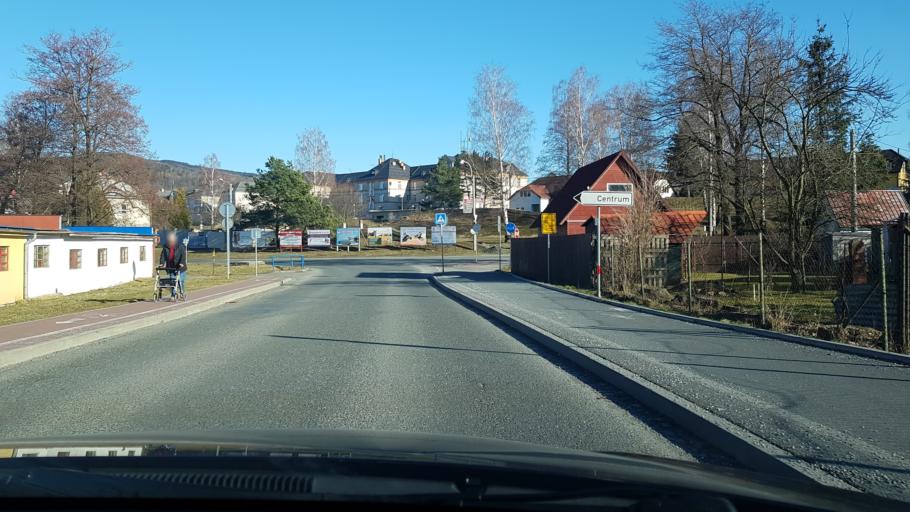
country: CZ
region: Olomoucky
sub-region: Okres Jesenik
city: Jesenik
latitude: 50.2215
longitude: 17.1913
